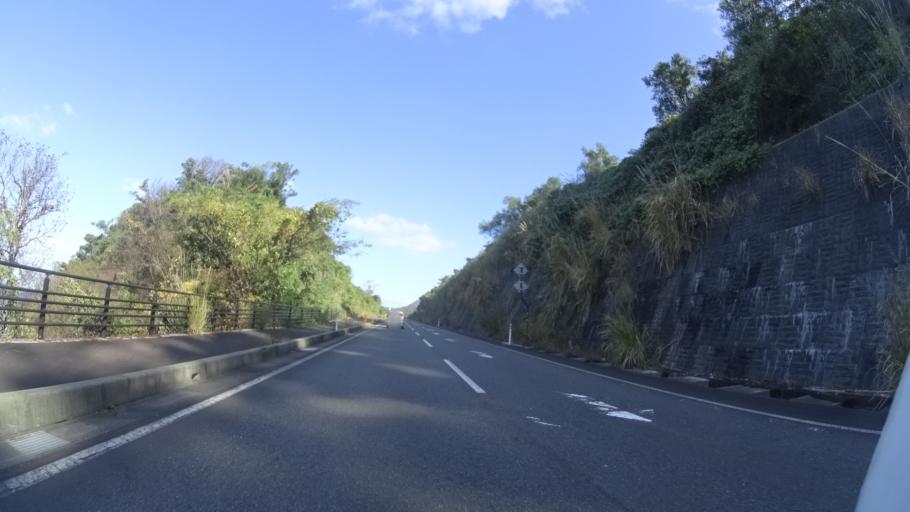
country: JP
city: Asahi
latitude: 35.9163
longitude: 135.9977
